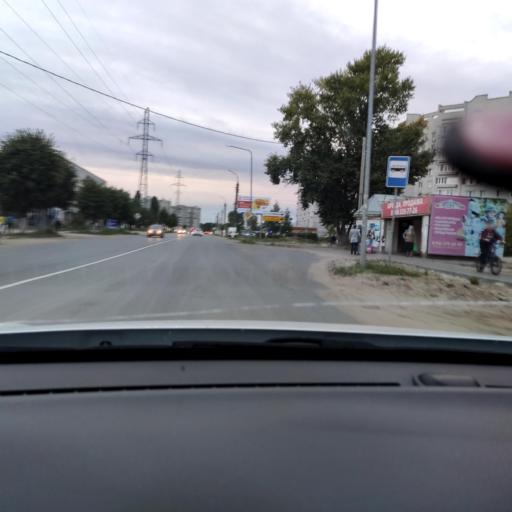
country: RU
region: Mariy-El
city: Volzhsk
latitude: 55.8664
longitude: 48.3554
